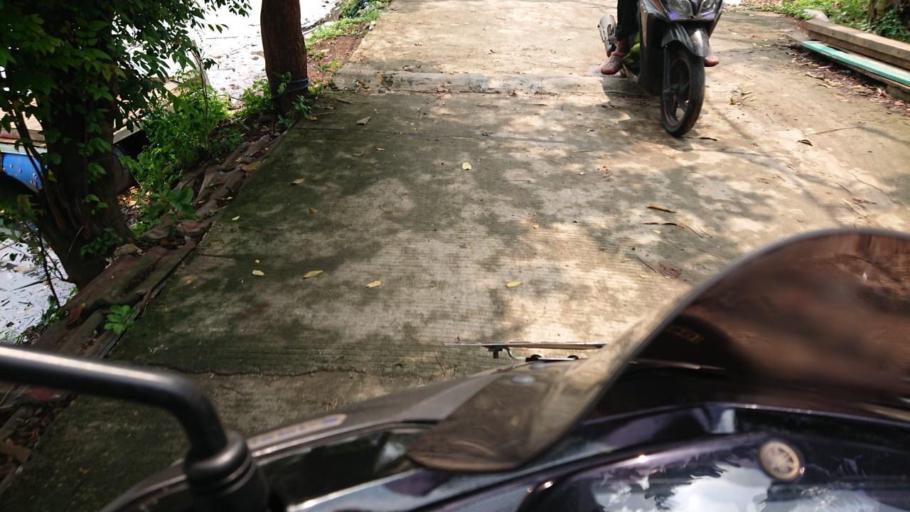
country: ID
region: West Java
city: Depok
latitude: -6.3556
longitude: 106.8687
